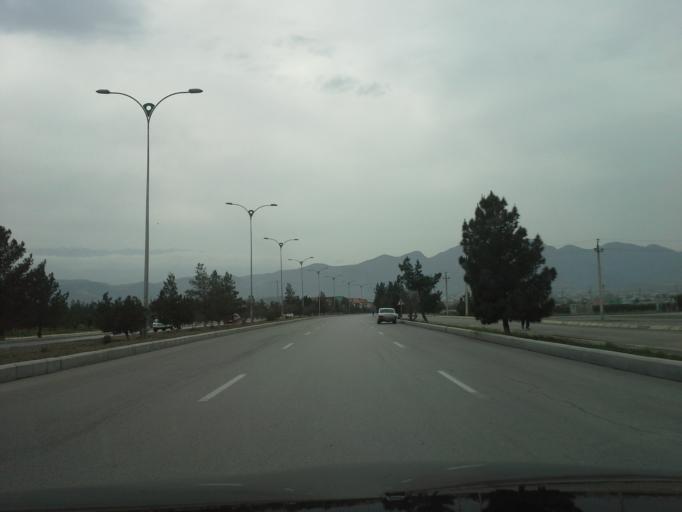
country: TM
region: Ahal
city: Abadan
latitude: 37.9684
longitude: 58.2303
